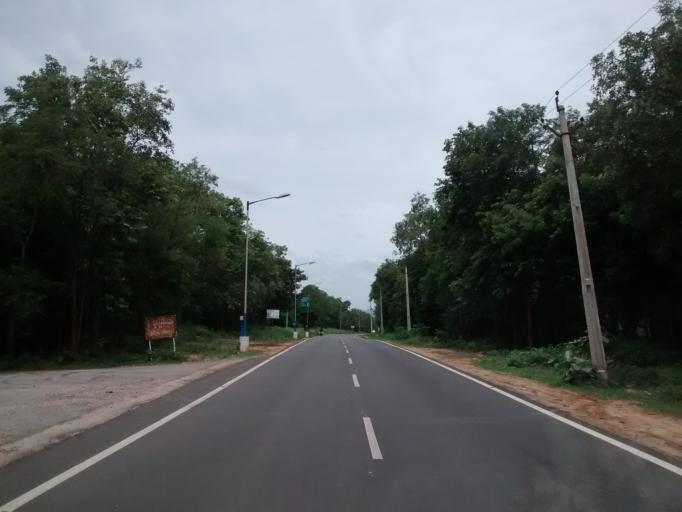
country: IN
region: Andhra Pradesh
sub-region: Chittoor
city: Tirupati
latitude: 13.6417
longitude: 79.3987
